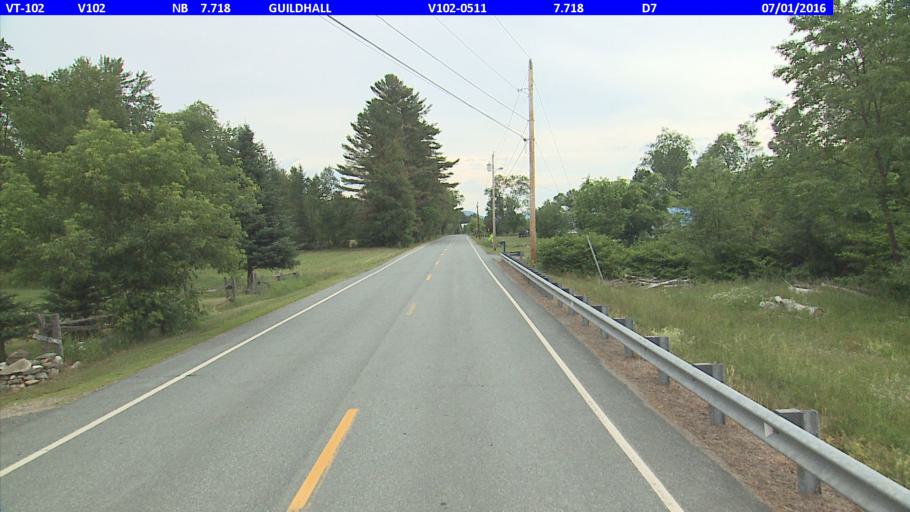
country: US
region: Vermont
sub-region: Essex County
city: Guildhall
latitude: 44.5707
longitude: -71.5580
